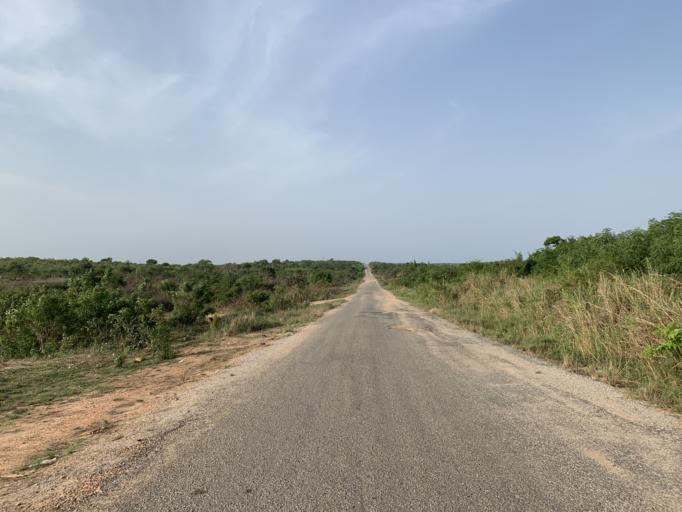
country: GH
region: Central
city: Winneba
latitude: 5.3809
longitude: -0.6086
